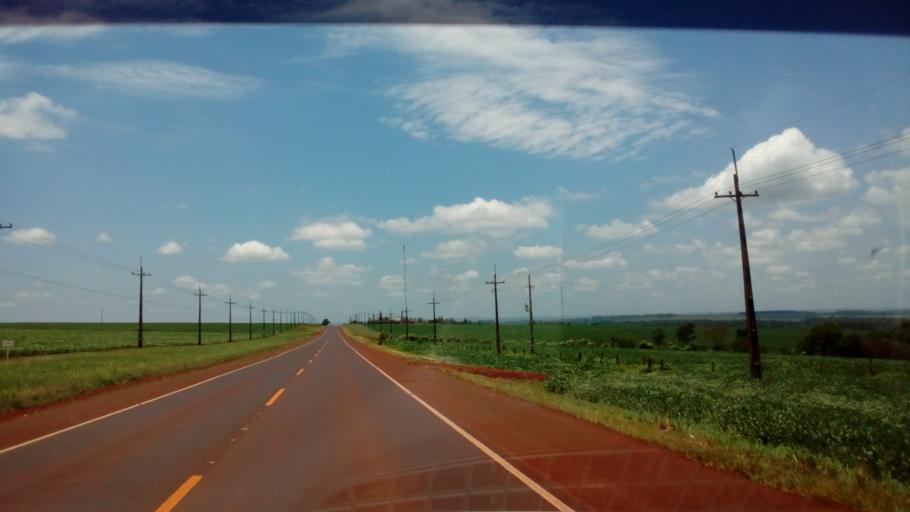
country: PY
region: Alto Parana
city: Naranjal
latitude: -26.0018
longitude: -55.1237
